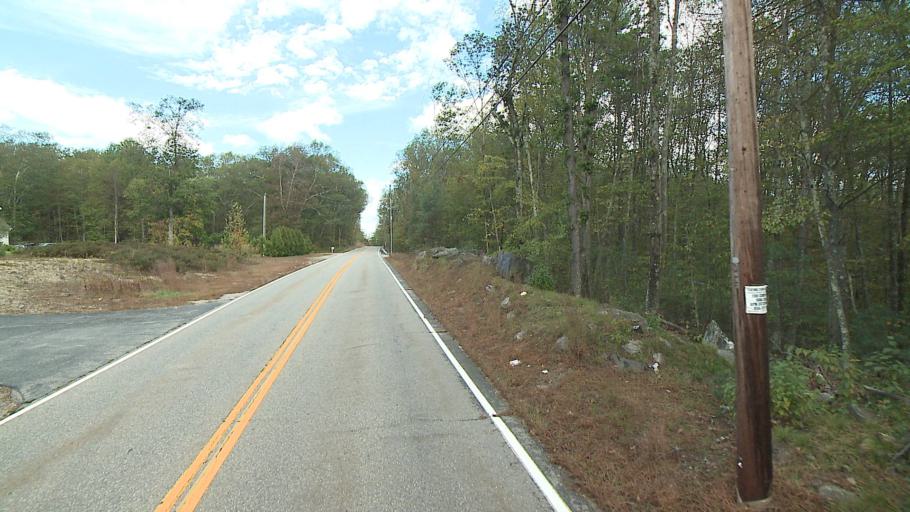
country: US
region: Massachusetts
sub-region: Worcester County
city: Webster
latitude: 42.0183
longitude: -71.8873
